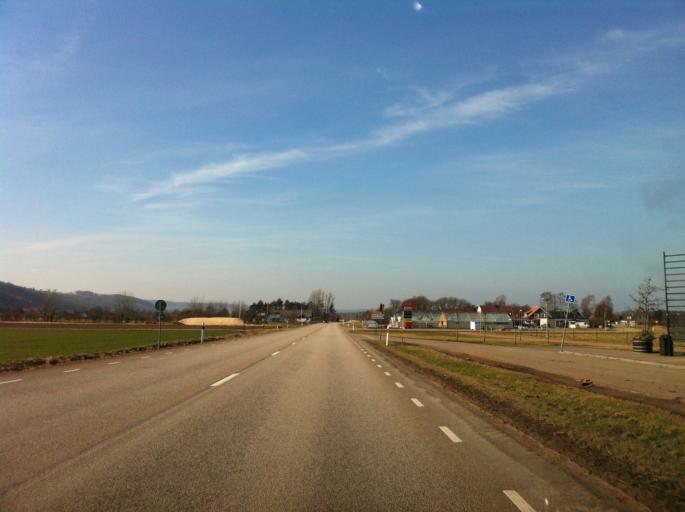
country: SE
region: Skane
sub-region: Bastads Kommun
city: Bastad
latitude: 56.4274
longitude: 12.9364
